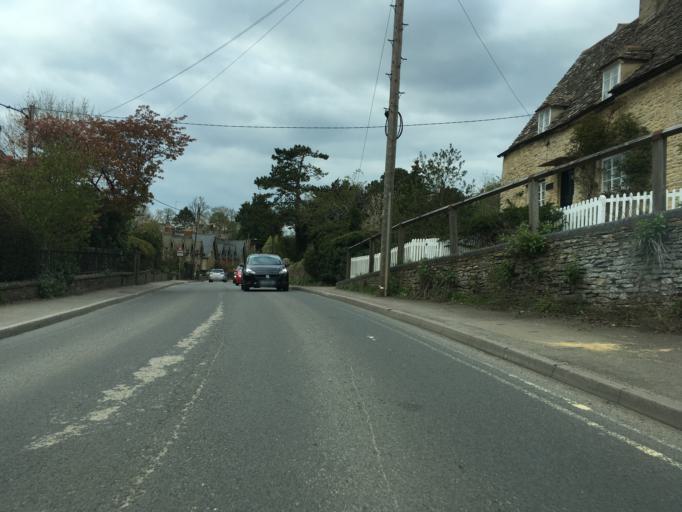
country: GB
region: England
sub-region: Oxfordshire
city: Woodstock
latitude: 51.8301
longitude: -1.3506
